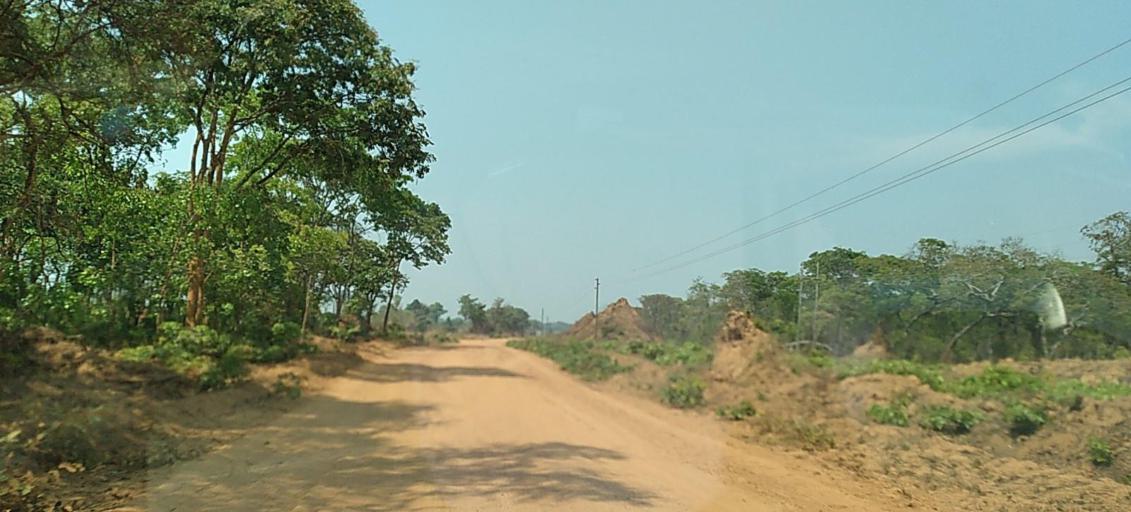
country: ZM
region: Copperbelt
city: Chingola
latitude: -13.0574
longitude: 27.4237
